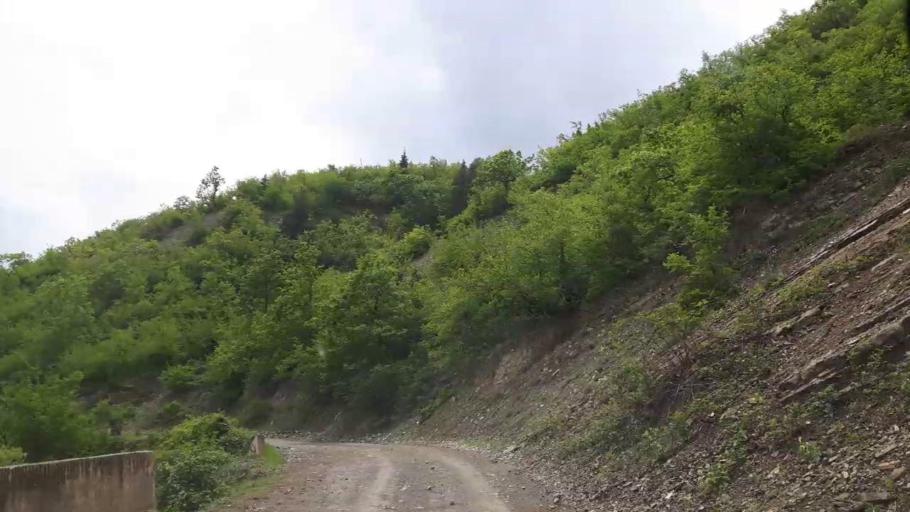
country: GE
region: Shida Kartli
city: Gori
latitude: 41.8860
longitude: 43.9979
